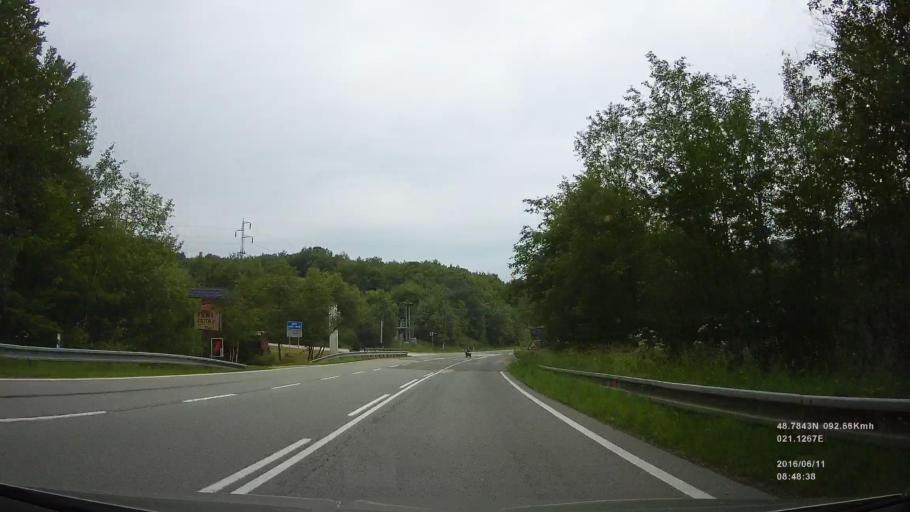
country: SK
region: Kosicky
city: Kosice
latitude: 48.7709
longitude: 21.1662
